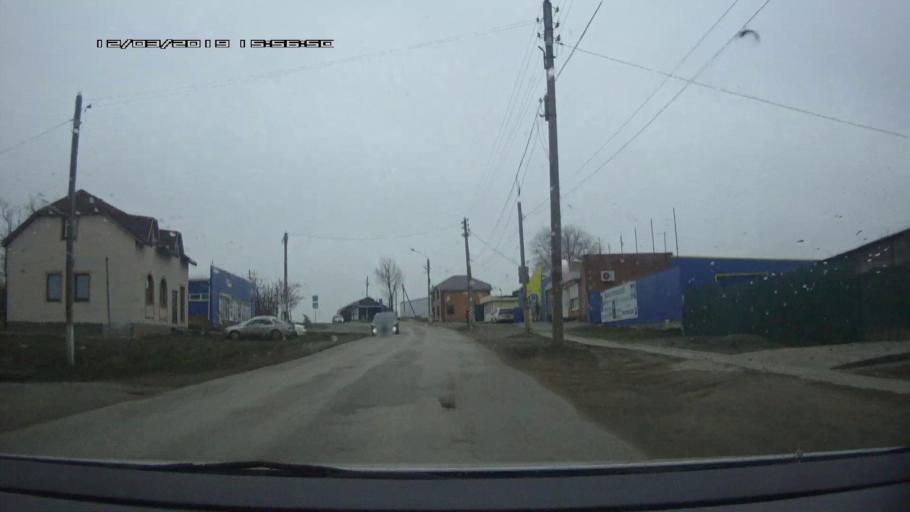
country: RU
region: Rostov
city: Novobataysk
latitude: 46.9025
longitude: 39.7820
